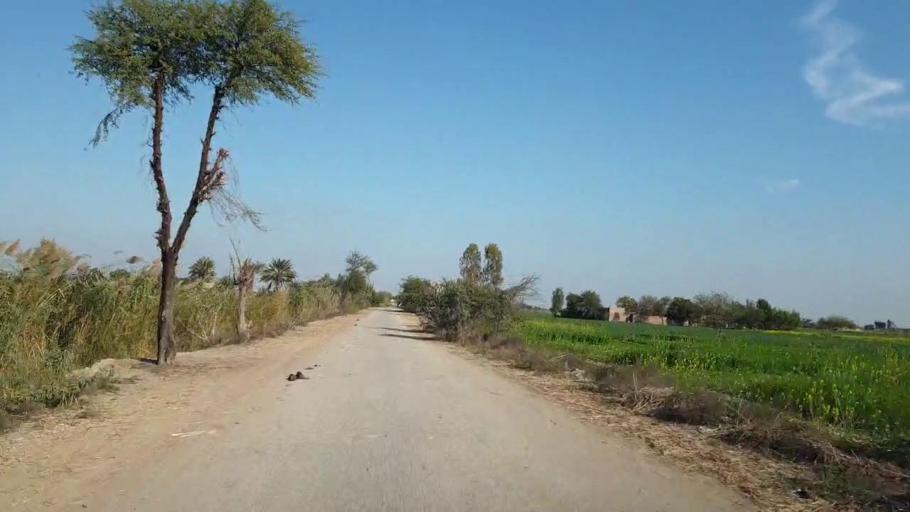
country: PK
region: Sindh
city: Khadro
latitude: 26.1898
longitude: 68.7574
